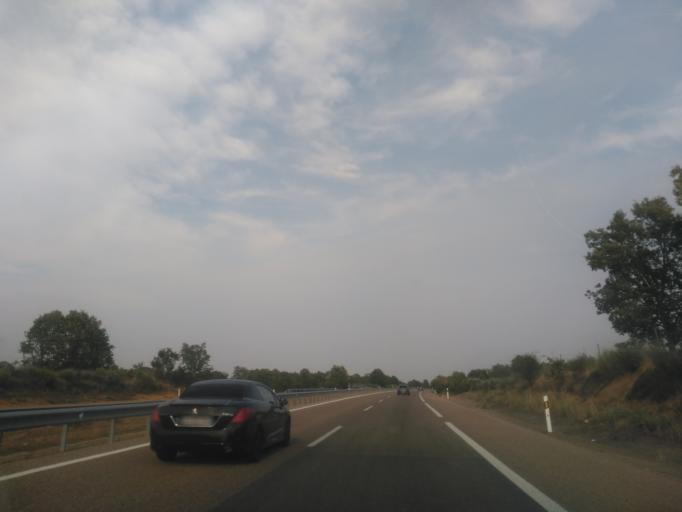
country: ES
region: Castille and Leon
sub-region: Provincia de Zamora
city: Mombuey
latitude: 42.0179
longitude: -6.3266
